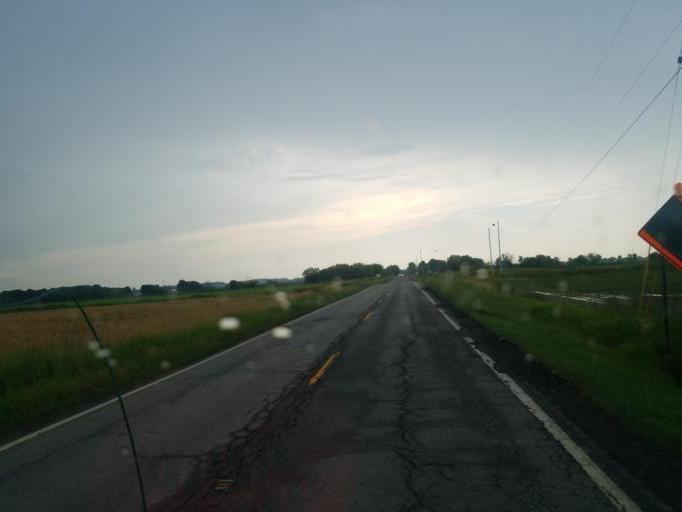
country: US
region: Ohio
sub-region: Wayne County
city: Rittman
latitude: 40.9458
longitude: -81.8078
